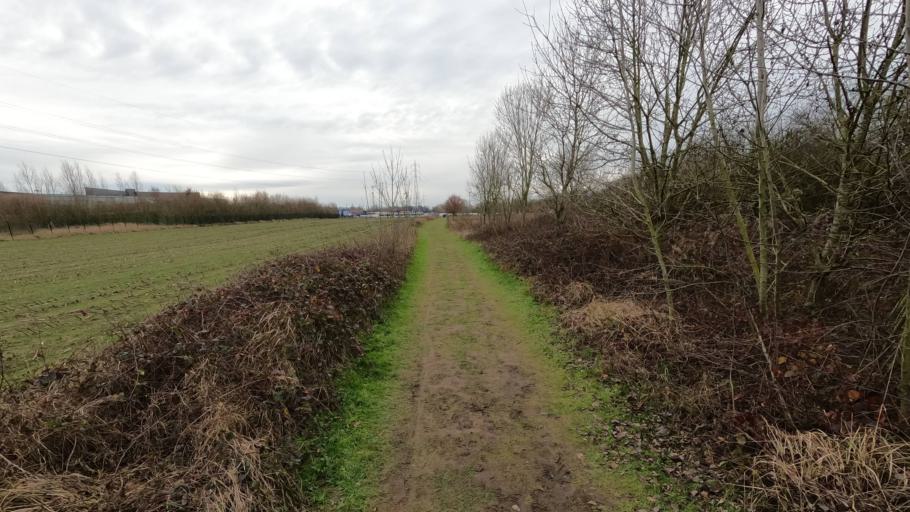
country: BE
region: Flanders
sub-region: Provincie Antwerpen
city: Wijnegem
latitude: 51.2249
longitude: 4.4939
